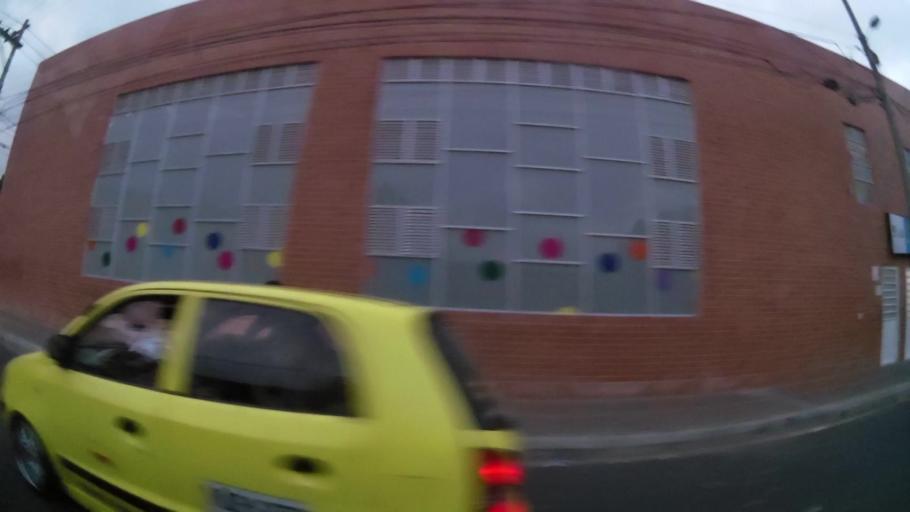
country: CO
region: Bogota D.C.
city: Bogota
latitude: 4.5828
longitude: -74.1319
